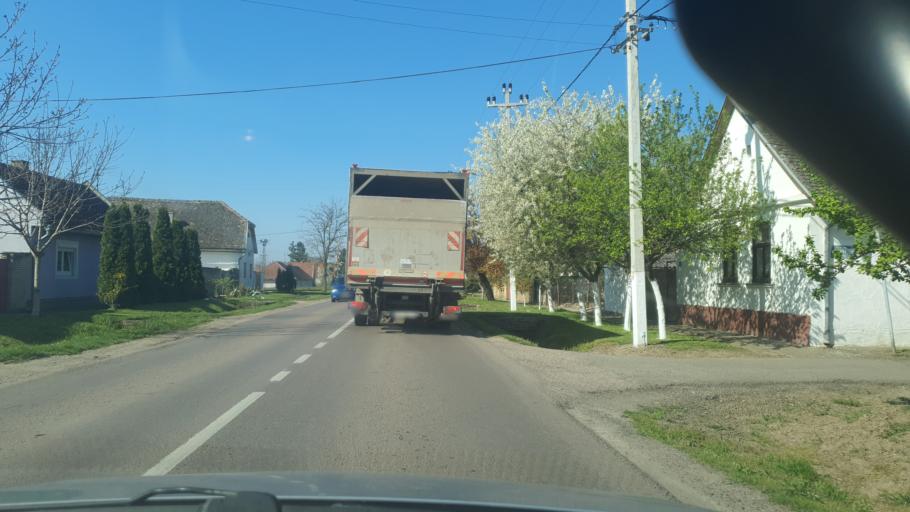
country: RS
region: Autonomna Pokrajina Vojvodina
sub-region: Zapadnobacki Okrug
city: Sombor
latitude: 45.7694
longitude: 19.2675
